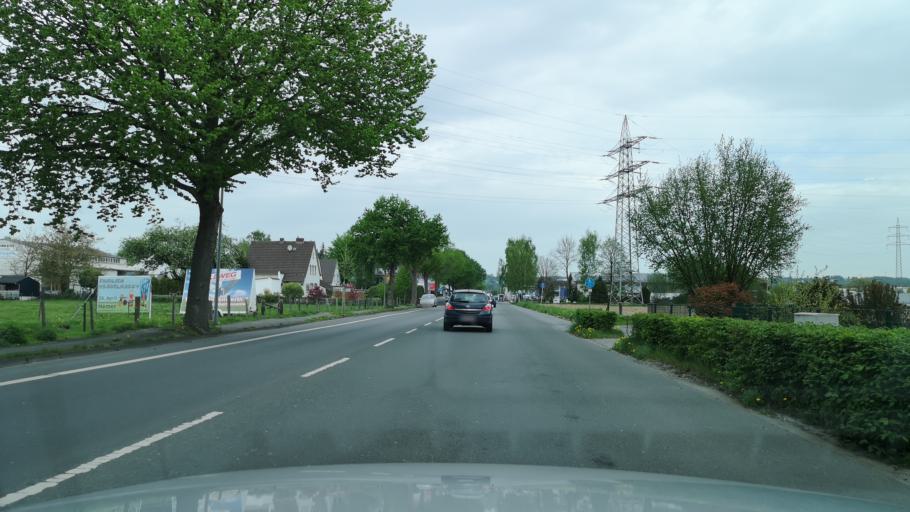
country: DE
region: North Rhine-Westphalia
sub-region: Regierungsbezirk Arnsberg
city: Menden
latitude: 51.4534
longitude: 7.7782
